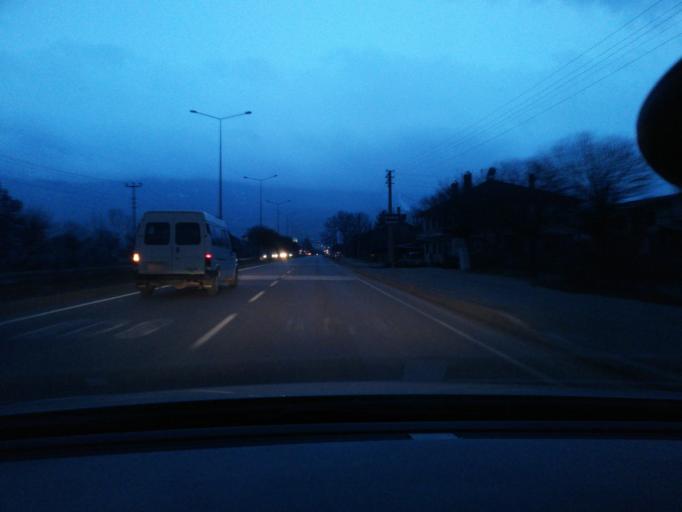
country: TR
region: Bolu
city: Bolu
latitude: 40.7072
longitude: 31.6171
